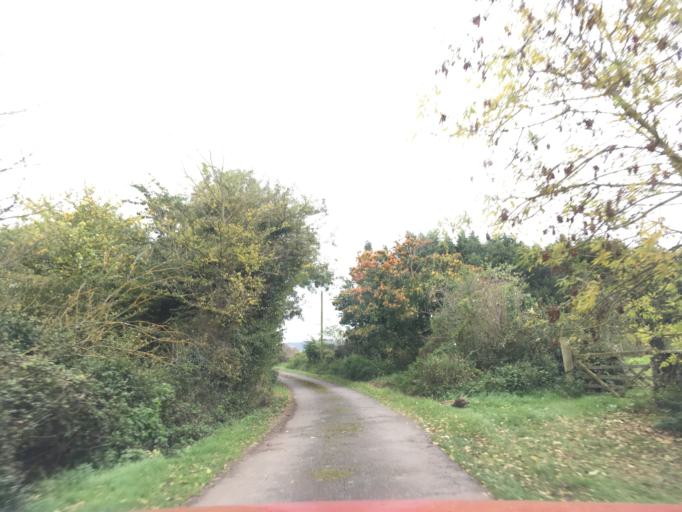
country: GB
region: England
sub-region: Gloucestershire
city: Stonehouse
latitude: 51.7536
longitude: -2.3041
